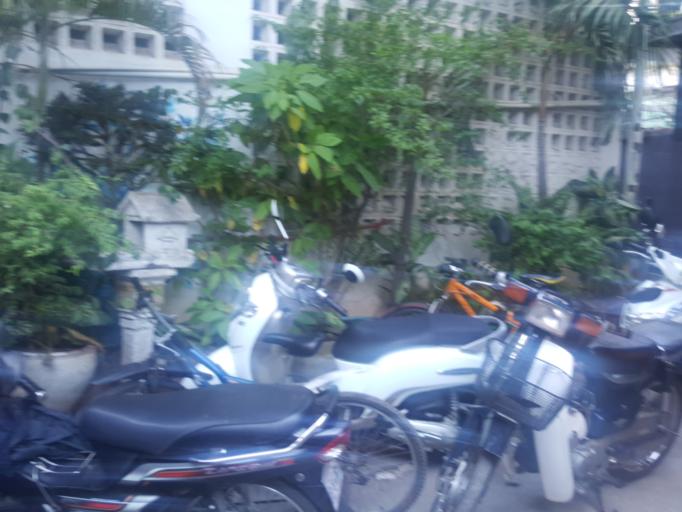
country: KH
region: Phnom Penh
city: Phnom Penh
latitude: 11.5603
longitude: 104.9304
